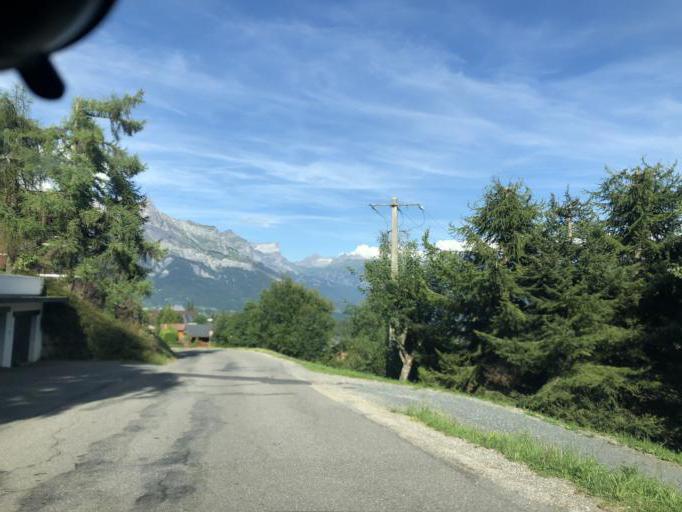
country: FR
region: Rhone-Alpes
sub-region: Departement de la Haute-Savoie
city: Cordon
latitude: 45.9089
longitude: 6.5954
